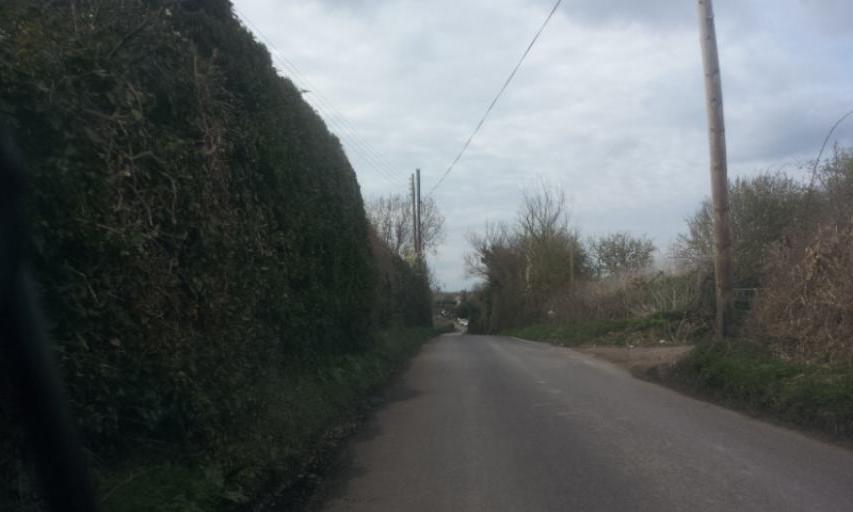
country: GB
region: England
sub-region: Kent
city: Teynham
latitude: 51.3258
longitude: 0.8307
